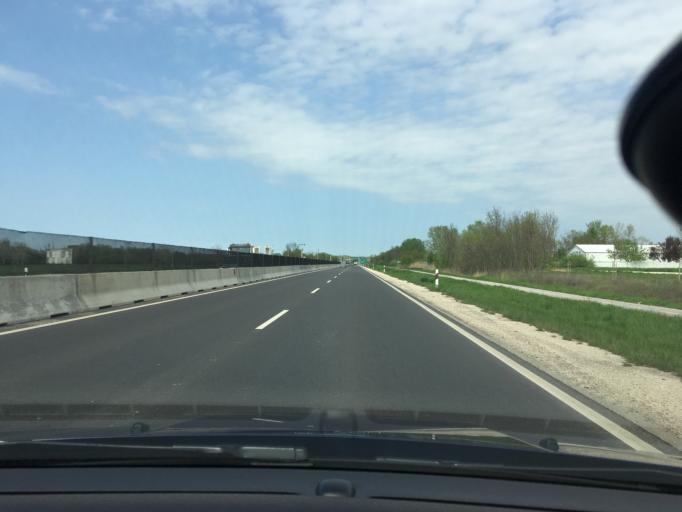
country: HU
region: Csongrad
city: Algyo
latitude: 46.3300
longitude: 20.1967
